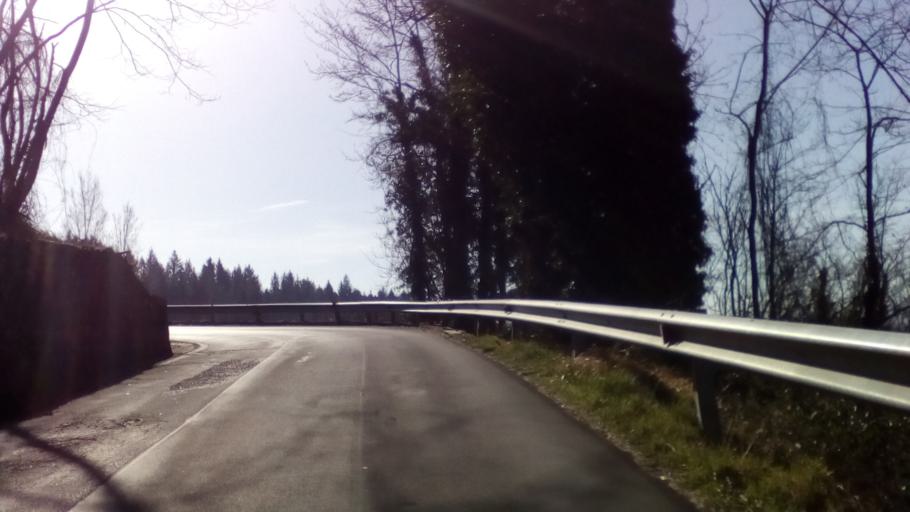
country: IT
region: Tuscany
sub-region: Provincia di Lucca
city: Castiglione di Garfagnana
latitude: 44.1404
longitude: 10.4271
